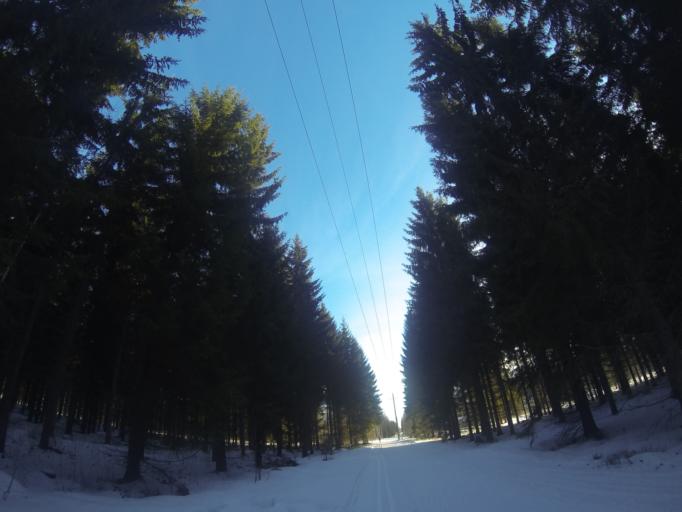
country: FI
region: Southern Savonia
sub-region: Savonlinna
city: Savonlinna
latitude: 61.9252
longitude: 28.8973
